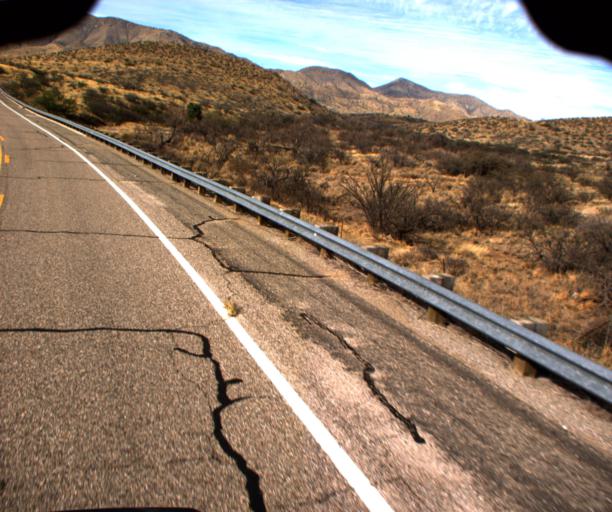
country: US
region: Arizona
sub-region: Cochise County
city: Willcox
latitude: 32.1446
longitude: -109.5650
